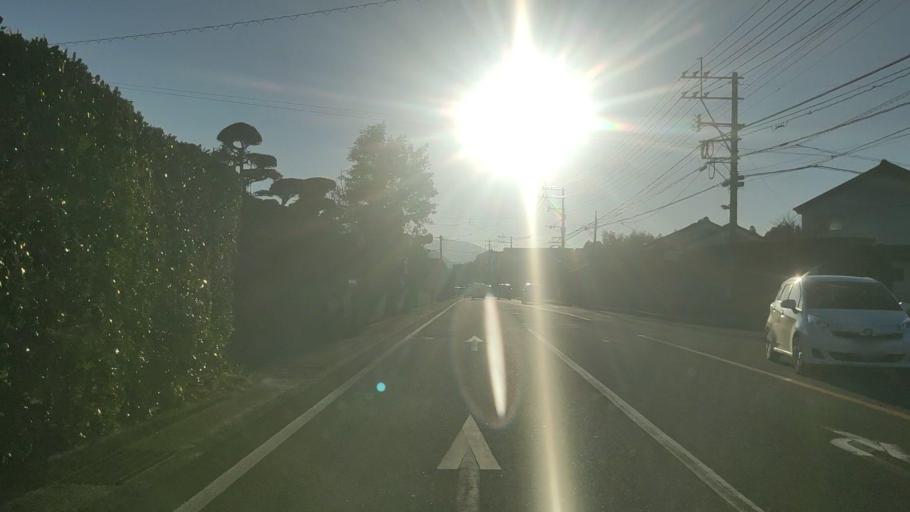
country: JP
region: Miyazaki
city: Miyazaki-shi
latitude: 31.8575
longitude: 131.3666
